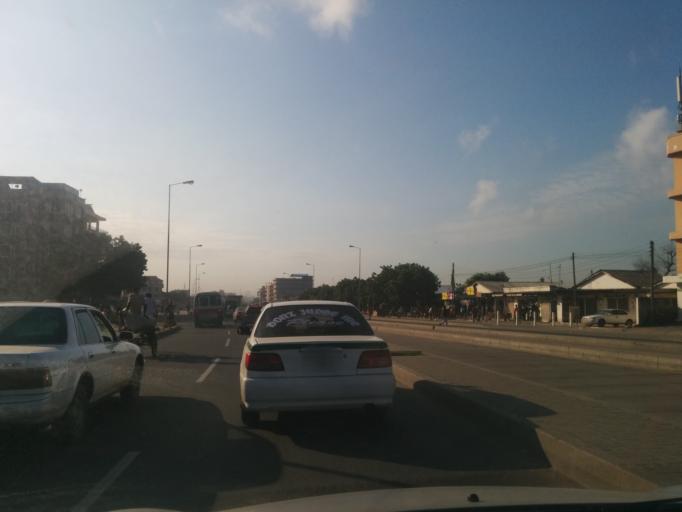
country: TZ
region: Dar es Salaam
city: Magomeni
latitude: -6.7986
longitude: 39.2326
